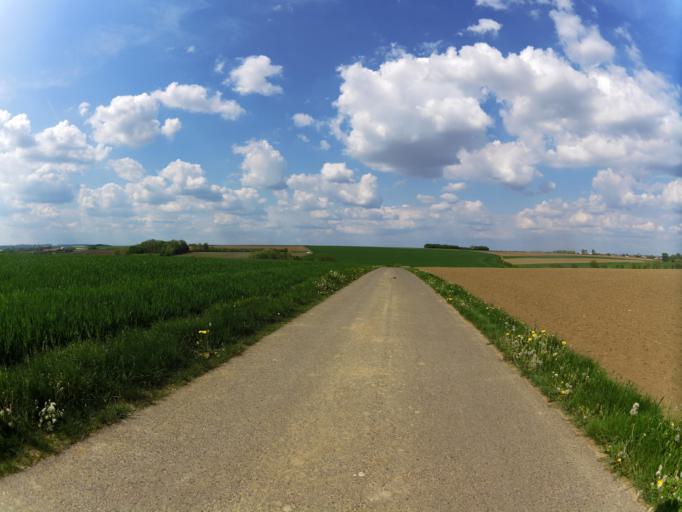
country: DE
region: Bavaria
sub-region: Regierungsbezirk Unterfranken
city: Giebelstadt
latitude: 49.6200
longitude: 9.9305
